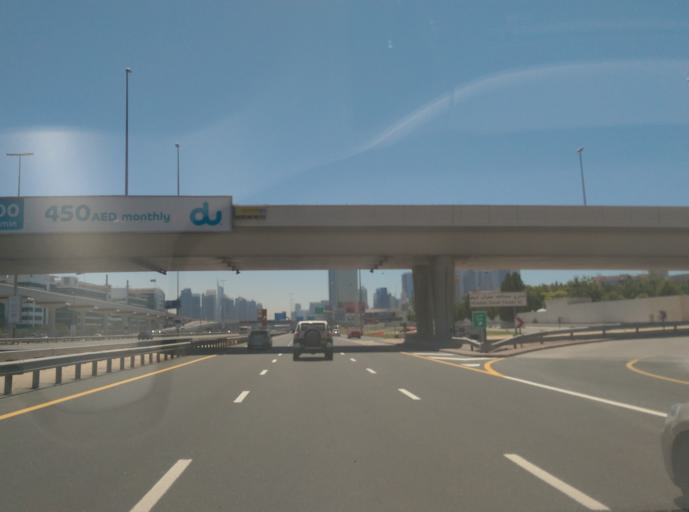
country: AE
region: Dubai
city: Dubai
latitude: 25.0992
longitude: 55.1689
